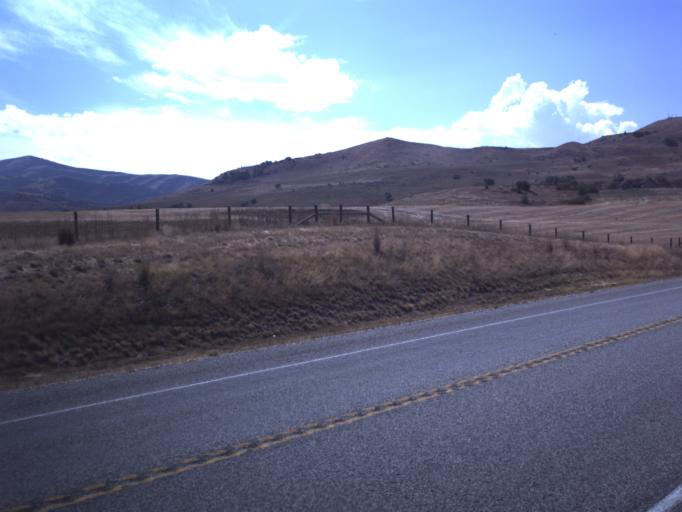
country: US
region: Utah
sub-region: Cache County
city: Mendon
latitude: 41.7555
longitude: -111.9993
